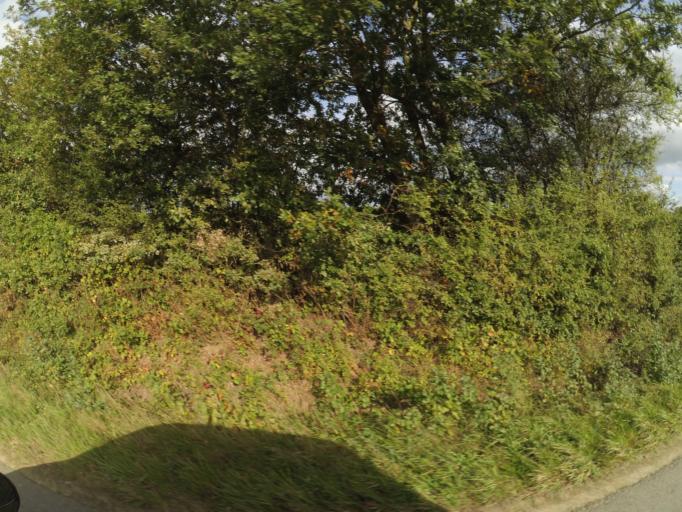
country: FR
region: Pays de la Loire
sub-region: Departement de la Loire-Atlantique
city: Fay-de-Bretagne
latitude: 47.4391
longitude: -1.8092
